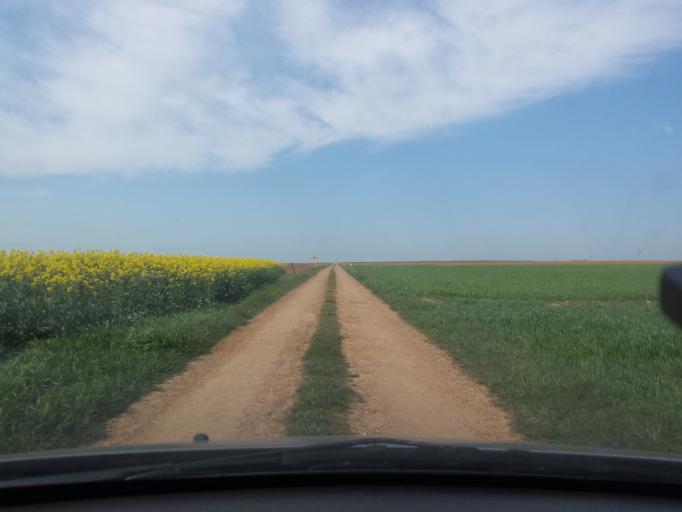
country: FR
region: Pays de la Loire
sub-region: Departement de la Vendee
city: Nalliers
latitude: 46.4866
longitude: -1.0671
